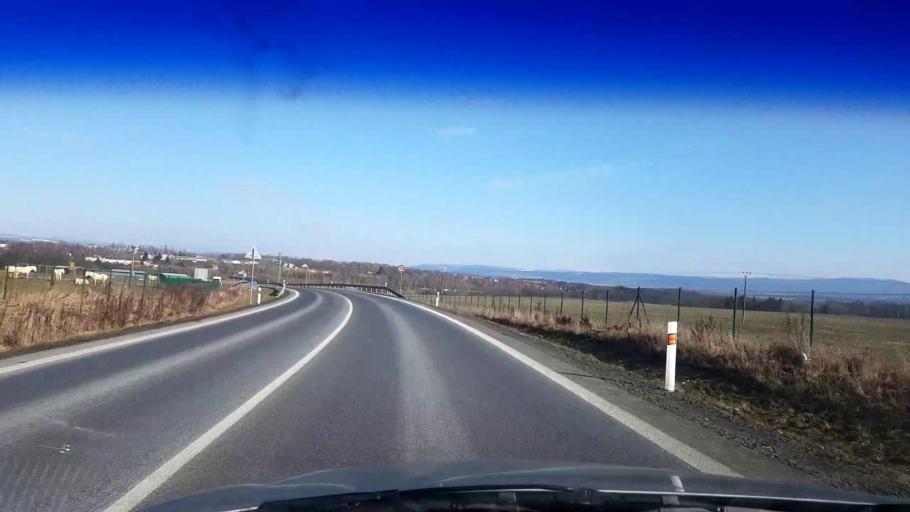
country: CZ
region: Karlovarsky
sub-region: Okres Cheb
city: Cheb
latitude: 50.0551
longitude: 12.3683
